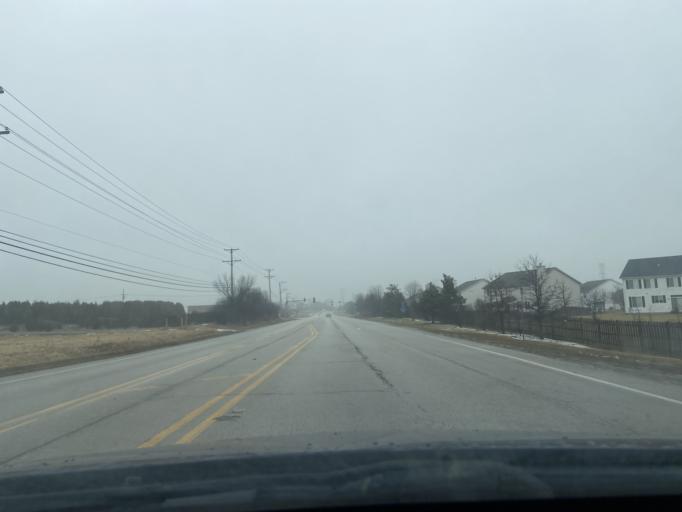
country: US
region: Illinois
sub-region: Lake County
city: Round Lake
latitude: 42.3139
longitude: -88.1013
